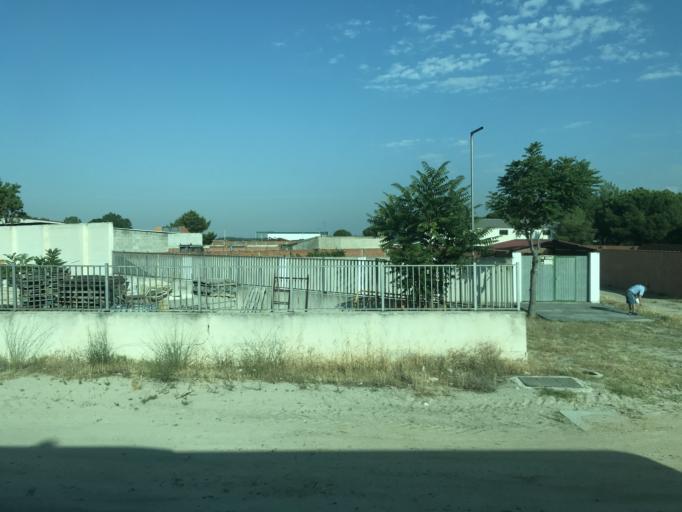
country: ES
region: Castille and Leon
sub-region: Provincia de Valladolid
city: Mojados
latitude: 41.4363
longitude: -4.6666
